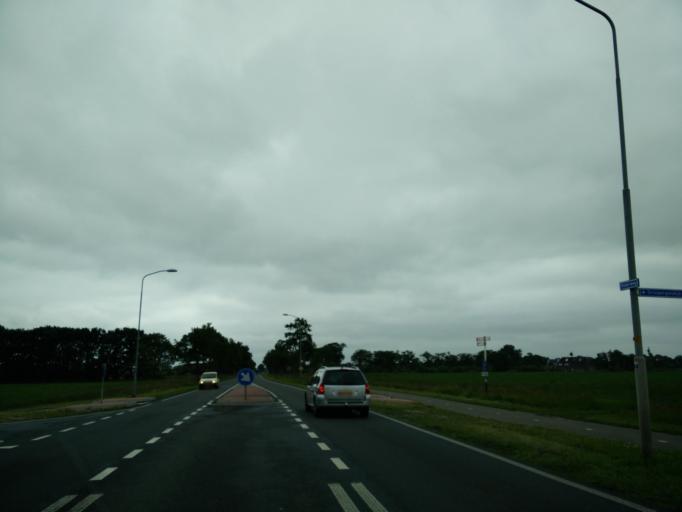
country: NL
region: Groningen
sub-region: Gemeente Leek
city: Leek
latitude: 53.1476
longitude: 6.4763
